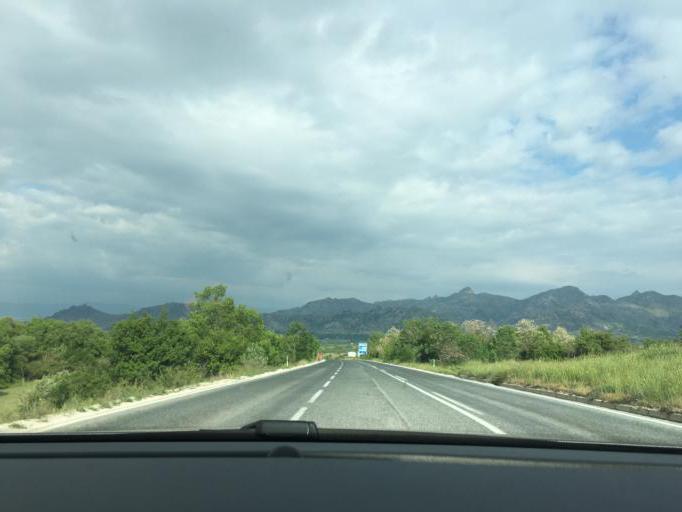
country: MK
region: Prilep
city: Prilep
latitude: 41.3696
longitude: 21.6273
